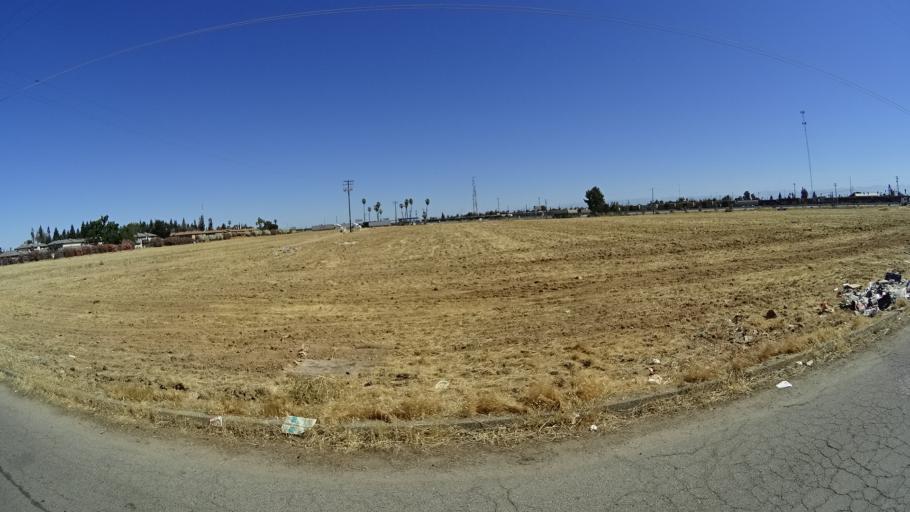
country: US
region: California
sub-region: Fresno County
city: West Park
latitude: 36.7754
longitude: -119.8466
